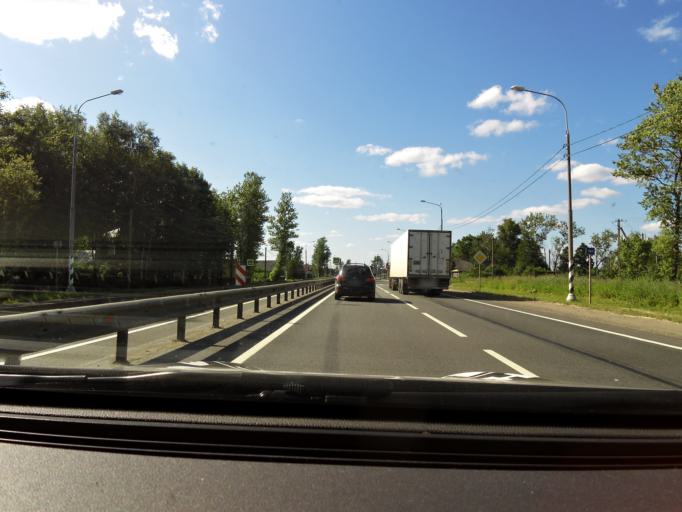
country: RU
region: Novgorod
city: Chudovo
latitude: 59.1379
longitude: 31.6266
